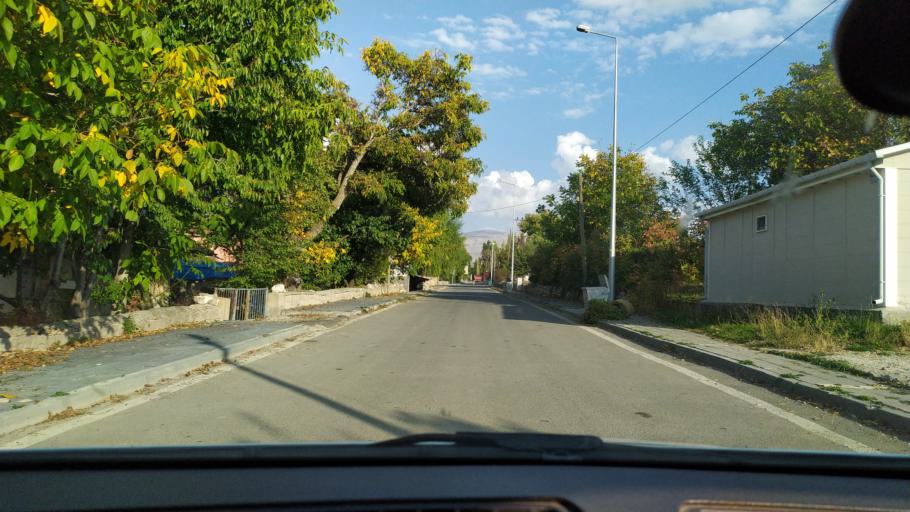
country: TR
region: Kayseri
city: Akkisla
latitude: 38.9998
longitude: 36.1665
